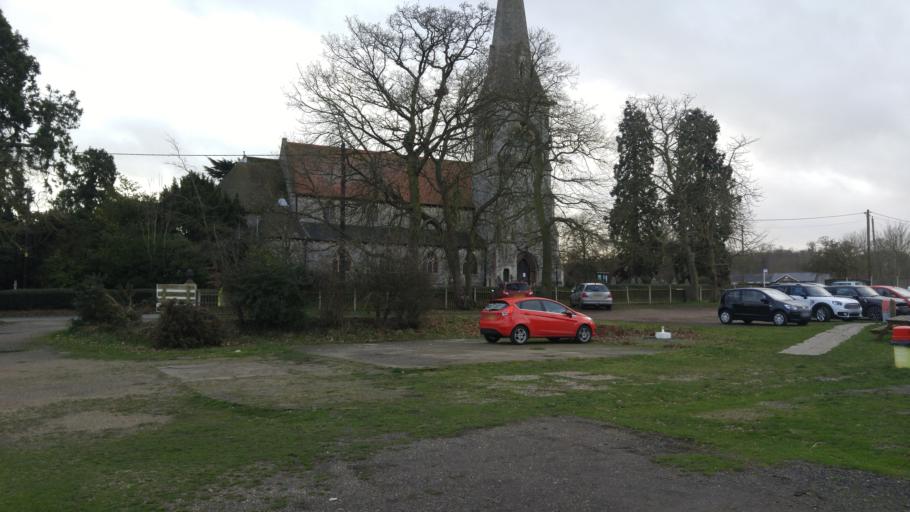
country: GB
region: England
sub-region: Essex
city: Mistley
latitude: 51.9450
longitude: 1.0742
